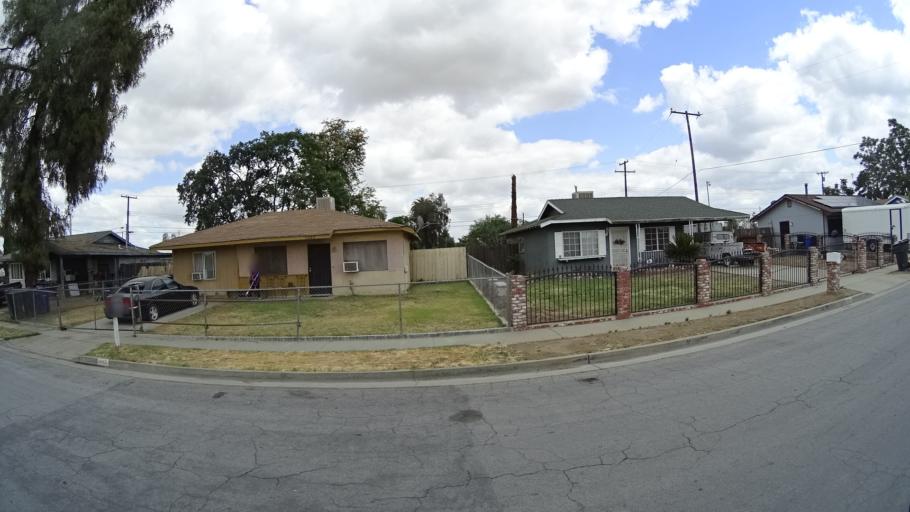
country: US
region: California
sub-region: Kings County
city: Home Garden
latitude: 36.3119
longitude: -119.6394
